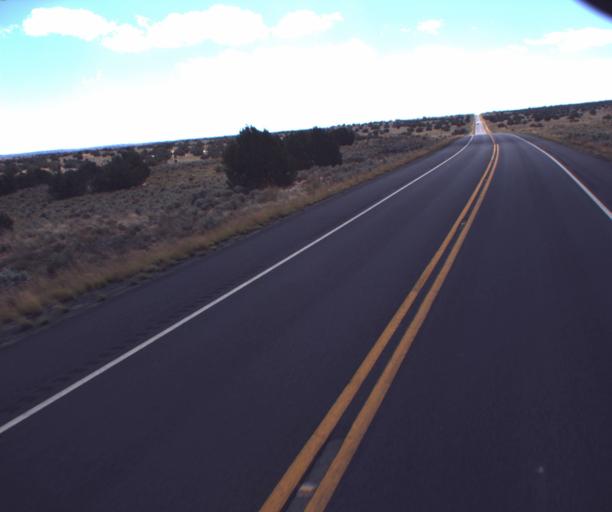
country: US
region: Arizona
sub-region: Apache County
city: Houck
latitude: 35.1683
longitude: -109.3382
